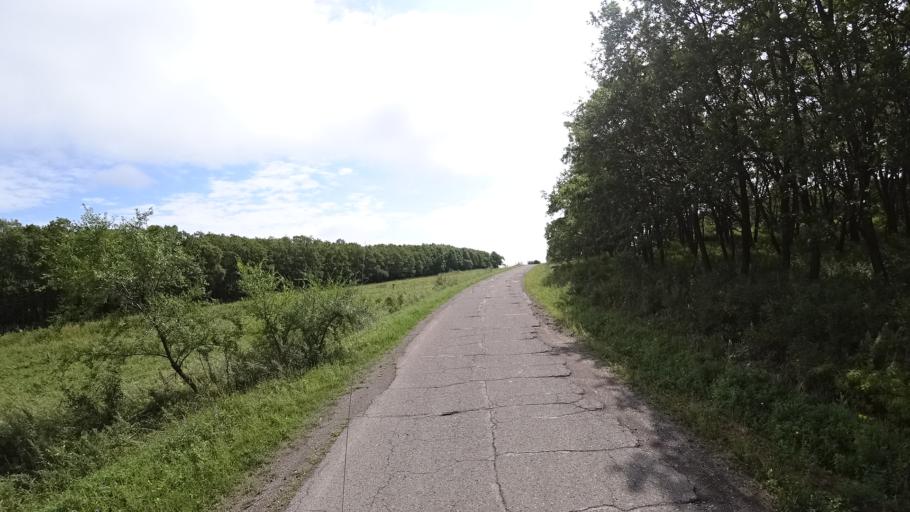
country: RU
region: Primorskiy
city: Lyalichi
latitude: 44.1462
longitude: 132.3902
